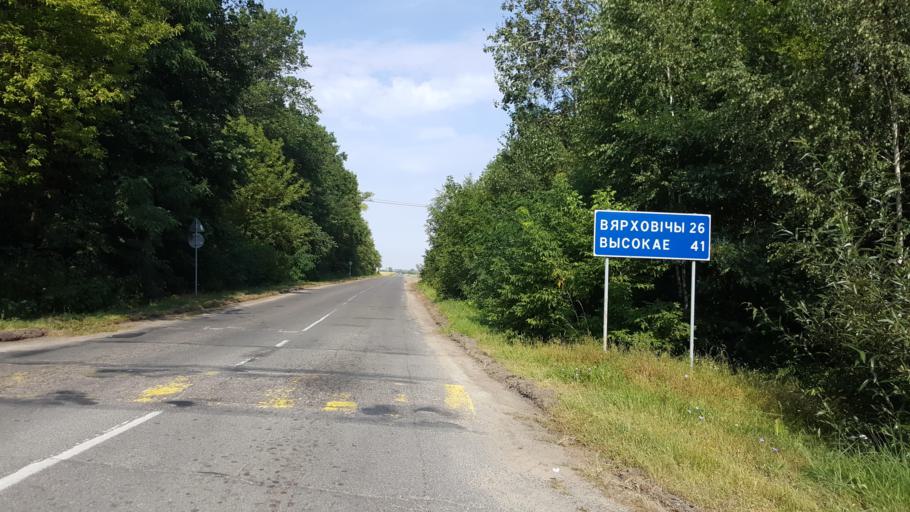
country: BY
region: Brest
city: Kamyanyets
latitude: 52.4127
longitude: 23.7880
